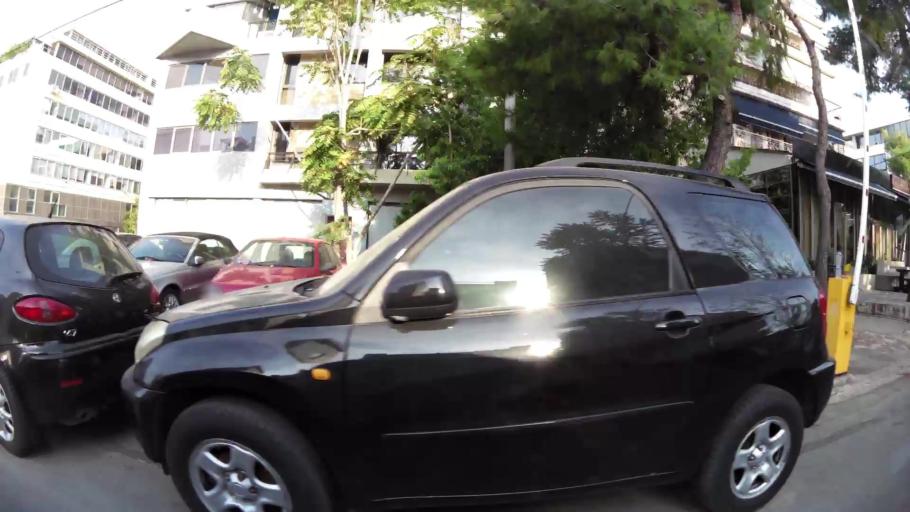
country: GR
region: Attica
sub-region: Nomarchia Athinas
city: Kallithea
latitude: 37.9417
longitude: 23.6990
